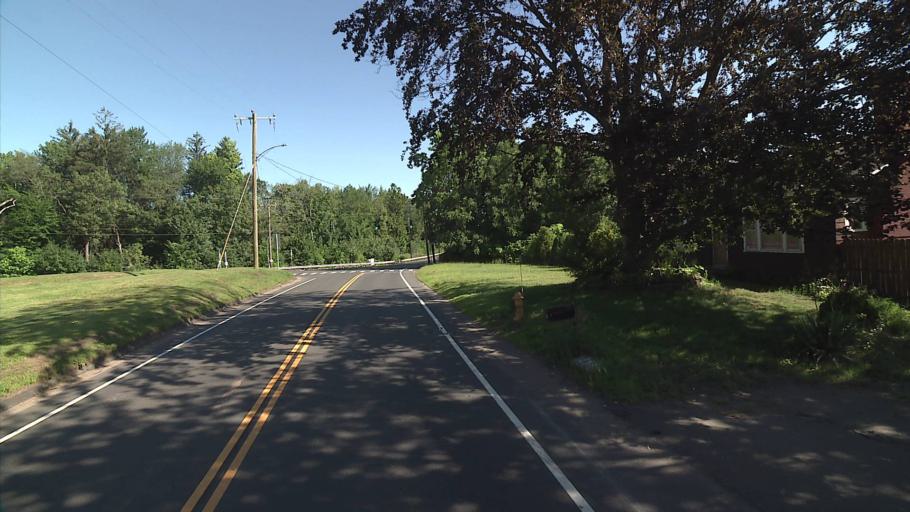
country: US
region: Connecticut
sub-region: New Haven County
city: Cheshire Village
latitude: 41.5701
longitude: -72.8963
